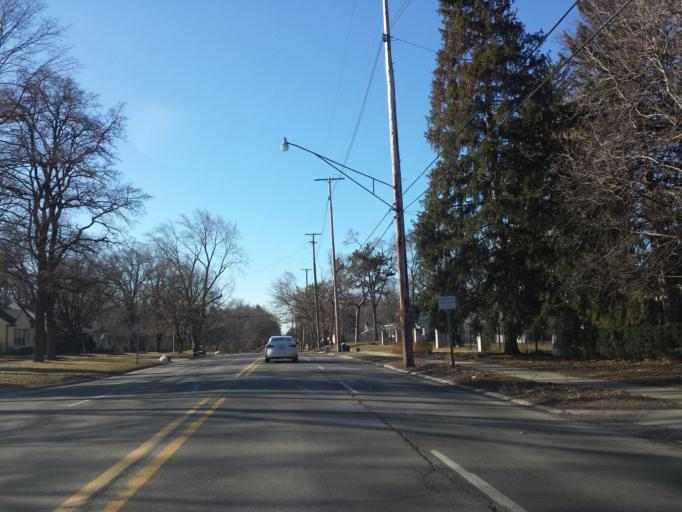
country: US
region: Michigan
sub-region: Oakland County
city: Clawson
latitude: 42.5131
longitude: -83.1453
